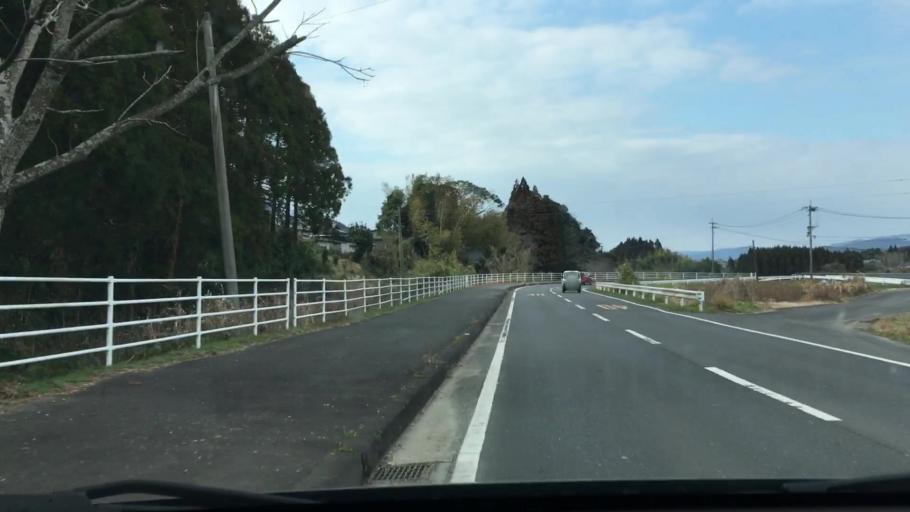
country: JP
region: Miyazaki
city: Kushima
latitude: 31.4980
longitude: 131.2389
